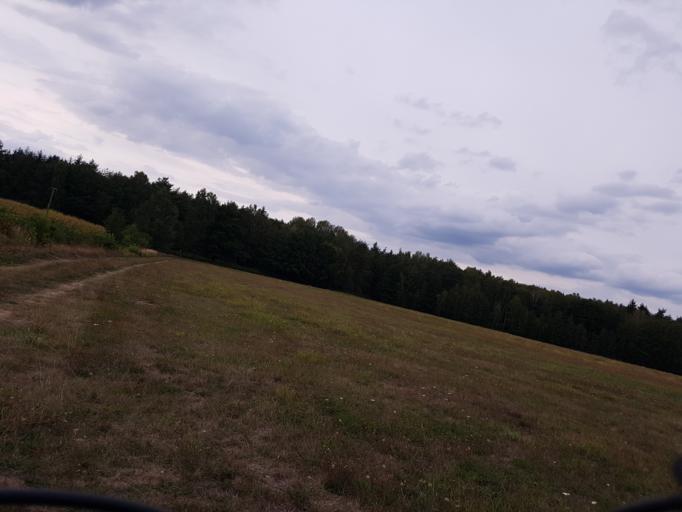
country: DE
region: Brandenburg
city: Trobitz
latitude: 51.5534
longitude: 13.4533
